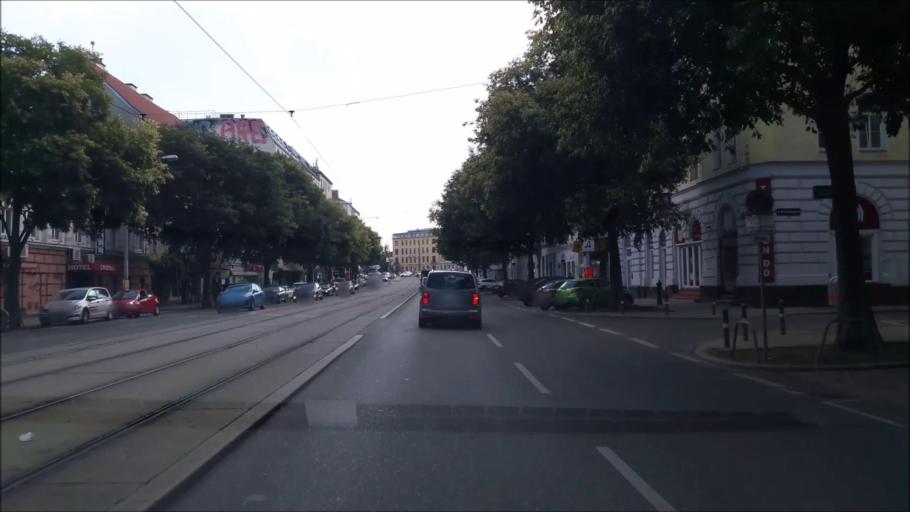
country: AT
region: Vienna
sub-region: Wien Stadt
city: Vienna
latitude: 48.2157
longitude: 16.3910
